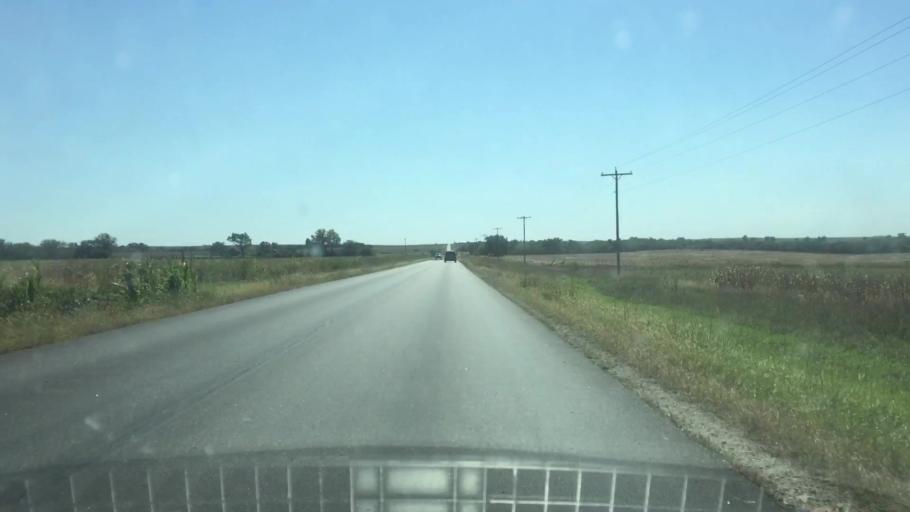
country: US
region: Kansas
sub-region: Marshall County
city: Marysville
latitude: 39.8900
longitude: -96.6010
